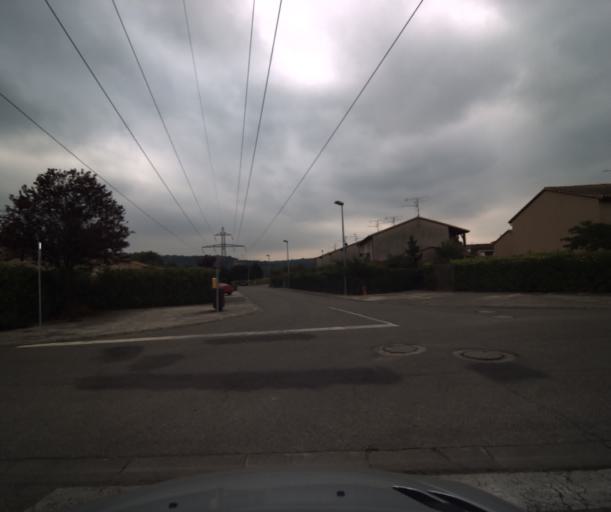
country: FR
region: Midi-Pyrenees
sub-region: Departement de la Haute-Garonne
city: Portet-sur-Garonne
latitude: 43.5311
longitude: 1.4146
